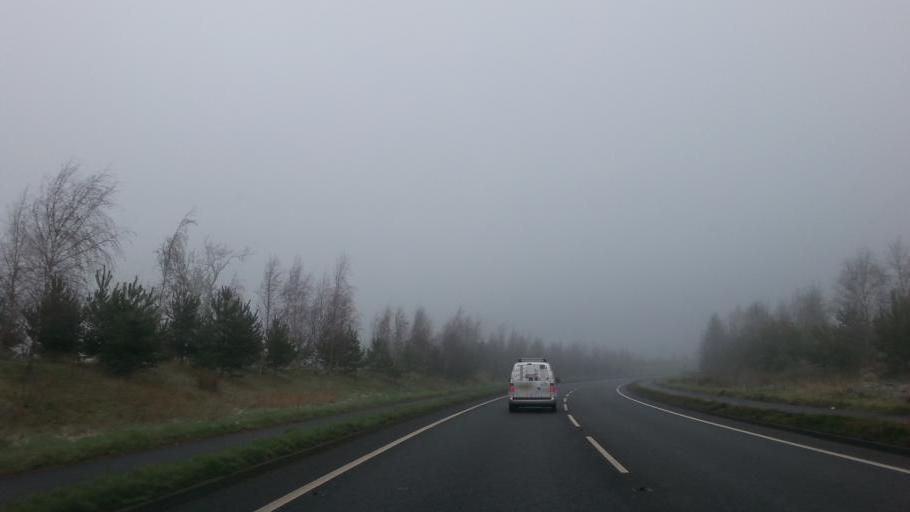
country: GB
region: England
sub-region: Cheshire East
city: Alderley Edge
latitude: 53.2903
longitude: -2.2549
